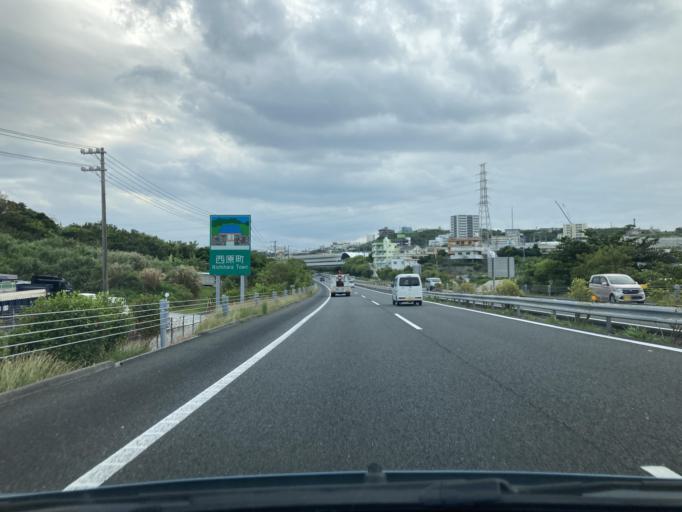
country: JP
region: Okinawa
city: Ginowan
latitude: 26.2444
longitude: 127.7456
